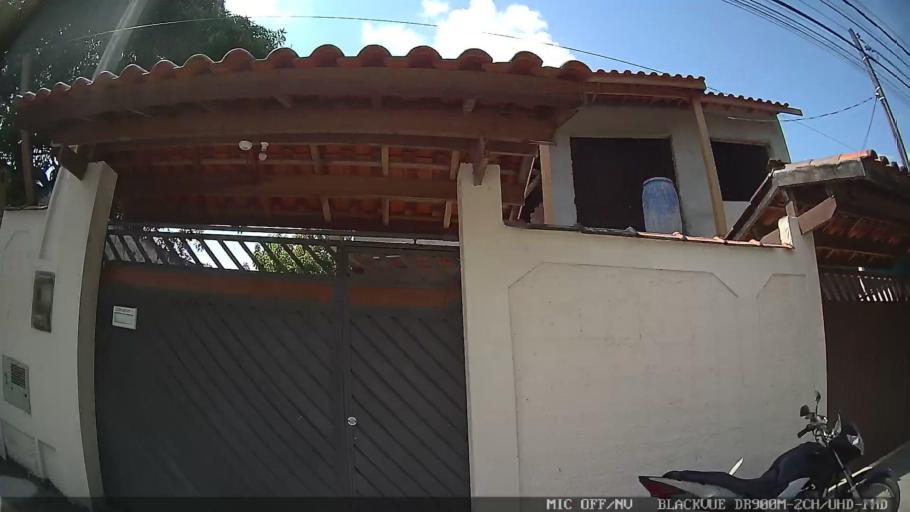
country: BR
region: Sao Paulo
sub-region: Caraguatatuba
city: Caraguatatuba
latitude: -23.6811
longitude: -45.4499
